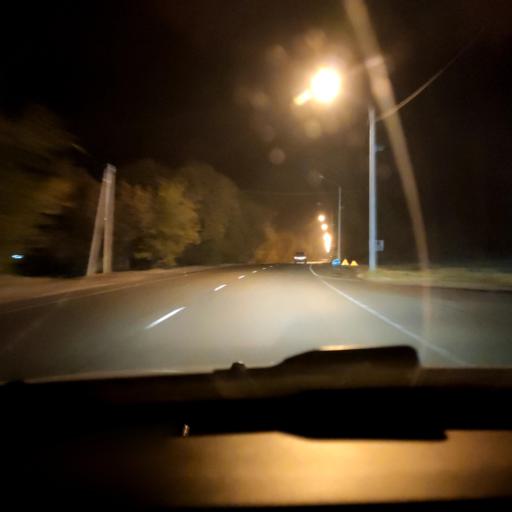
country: RU
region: Voronezj
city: Voronezh
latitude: 51.6151
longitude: 39.1787
